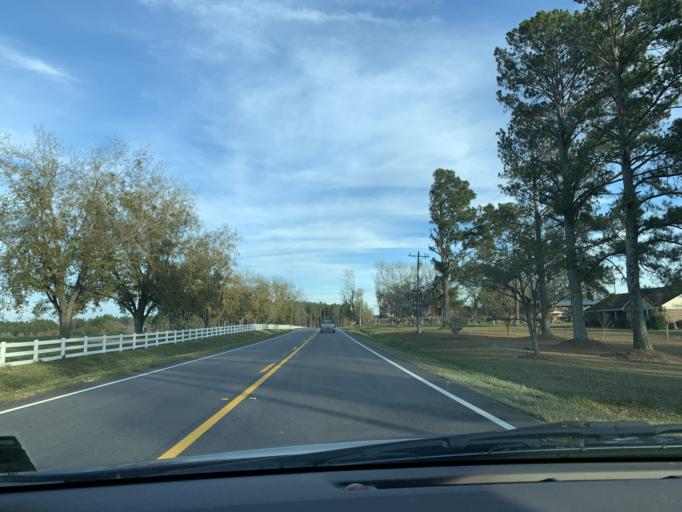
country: US
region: Georgia
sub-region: Irwin County
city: Ocilla
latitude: 31.5927
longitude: -83.2111
